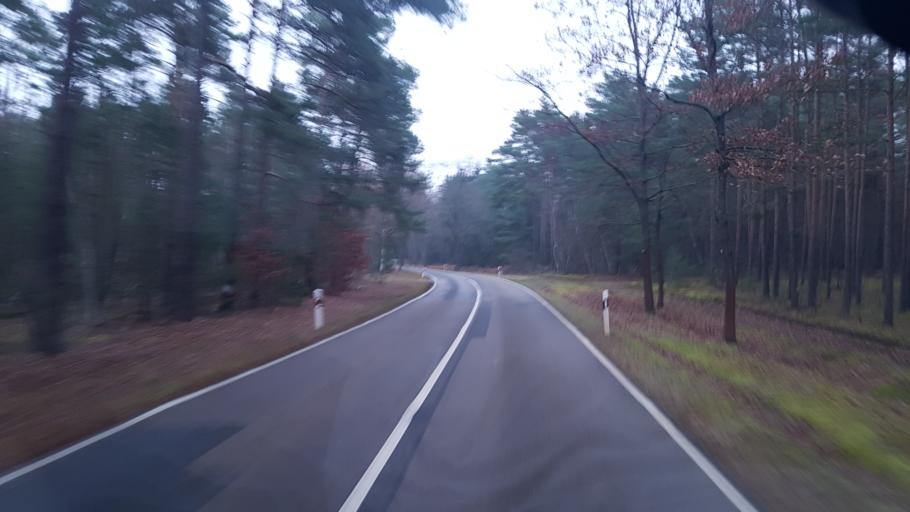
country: DE
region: Brandenburg
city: Drachhausen
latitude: 51.8724
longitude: 14.2766
